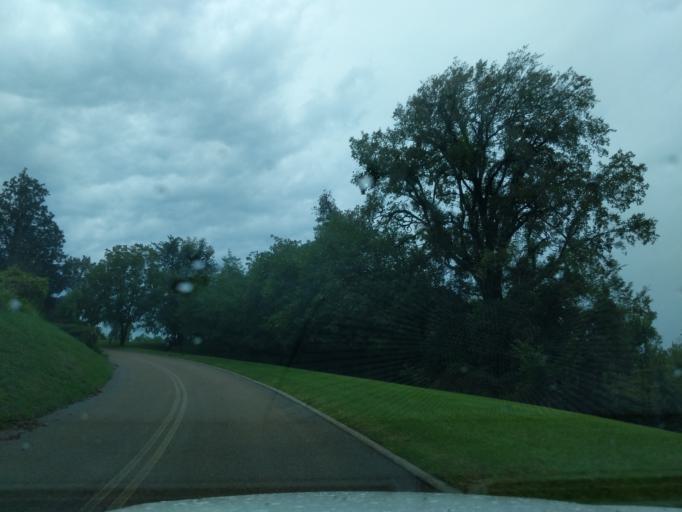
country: US
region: Mississippi
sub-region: Warren County
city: Vicksburg
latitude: 32.3685
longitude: -90.8705
